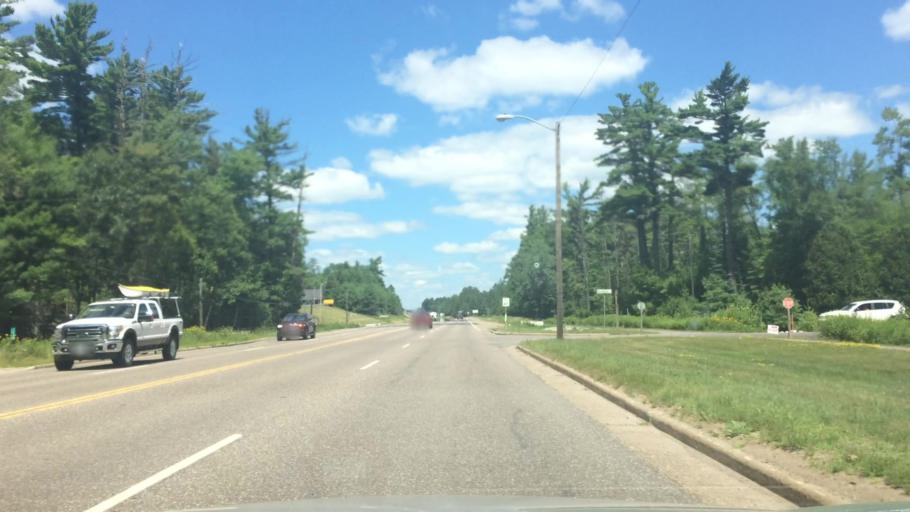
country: US
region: Wisconsin
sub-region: Vilas County
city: Lac du Flambeau
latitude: 45.9098
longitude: -89.6947
